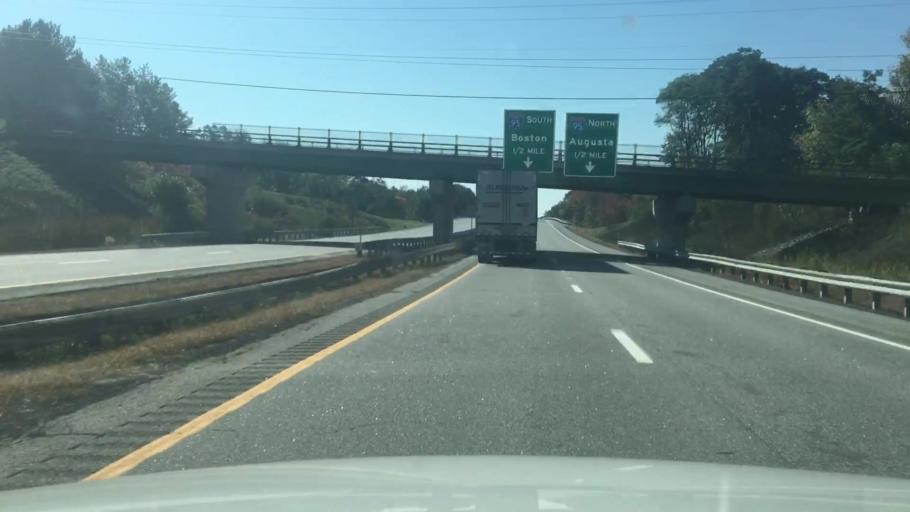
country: US
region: Maine
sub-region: Cumberland County
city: Falmouth
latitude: 43.7253
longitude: -70.2939
